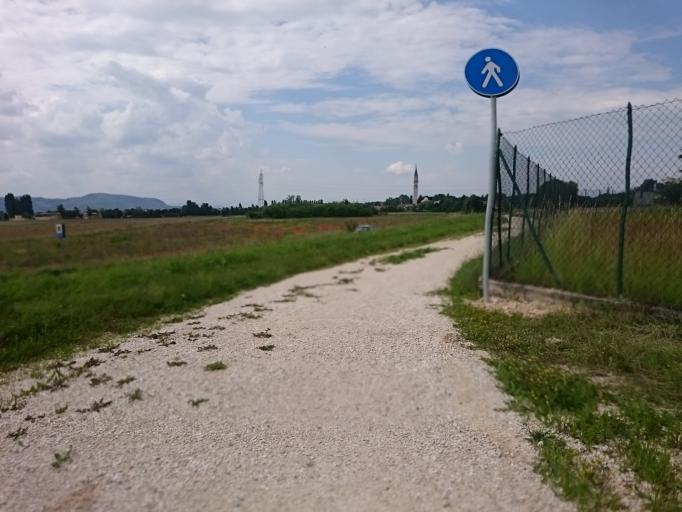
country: IT
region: Veneto
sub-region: Provincia di Vicenza
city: Montegaldella
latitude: 45.4297
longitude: 11.6777
